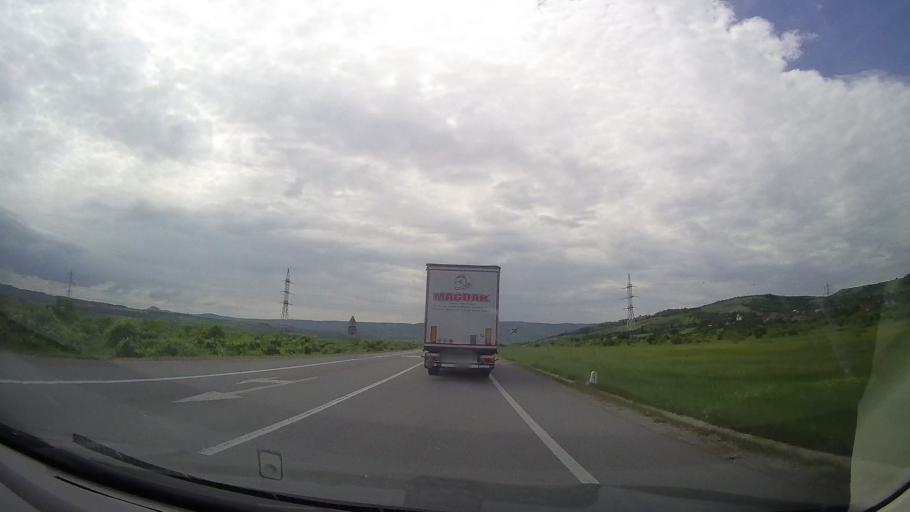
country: RS
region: Central Serbia
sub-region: Borski Okrug
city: Kladovo
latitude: 44.6352
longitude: 22.6047
